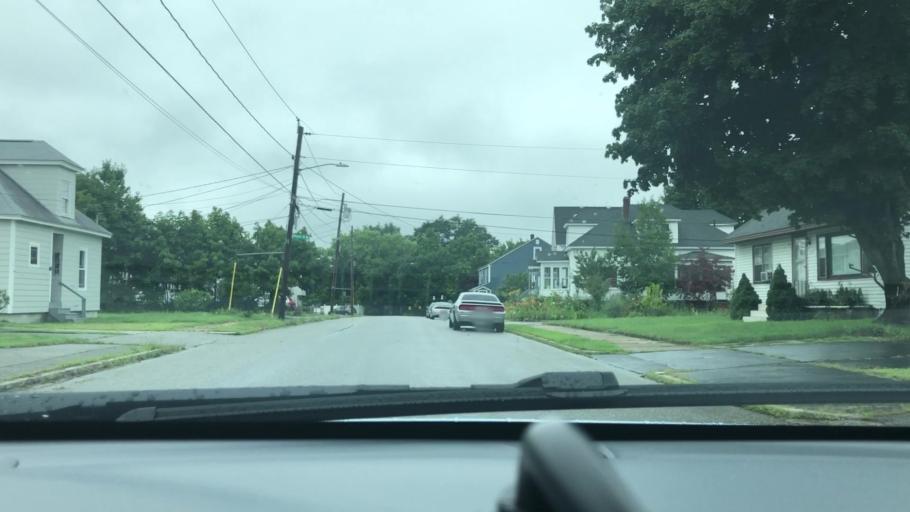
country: US
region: New Hampshire
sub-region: Hillsborough County
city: Pinardville
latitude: 42.9931
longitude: -71.4888
